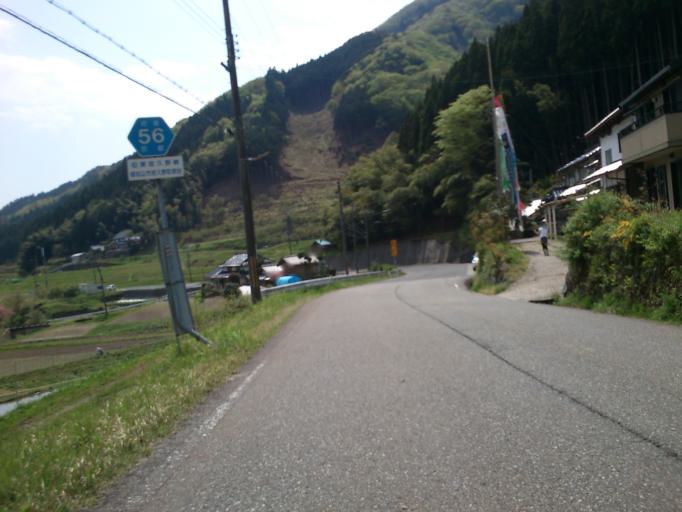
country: JP
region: Hyogo
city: Toyooka
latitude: 35.3916
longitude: 134.9419
